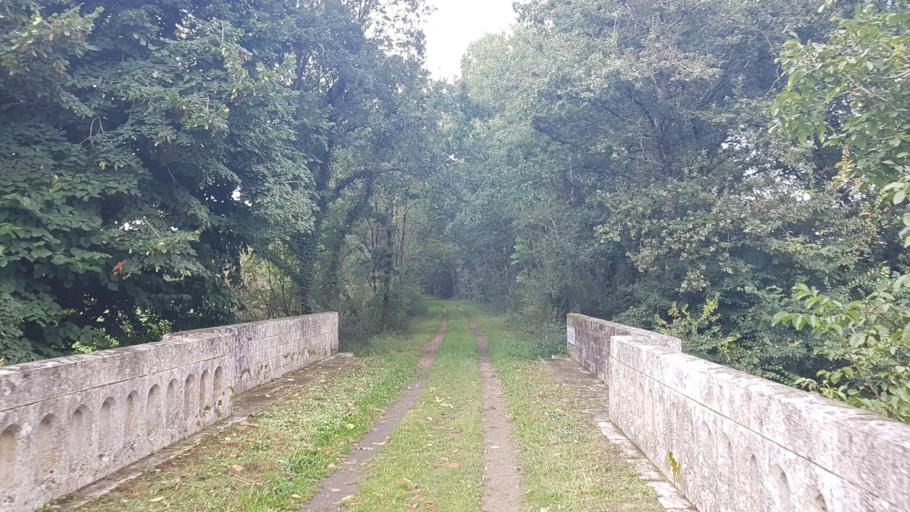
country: FR
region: Poitou-Charentes
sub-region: Departement de la Vienne
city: Saint-Savin
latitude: 46.5803
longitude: 0.8761
